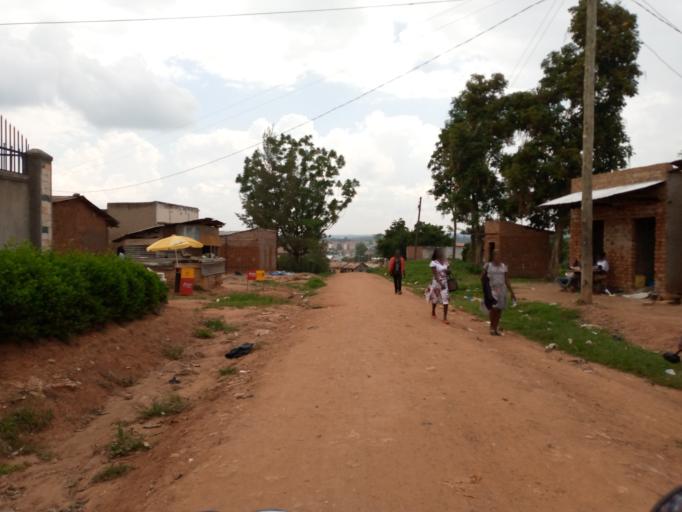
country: UG
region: Eastern Region
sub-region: Mbale District
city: Mbale
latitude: 1.0833
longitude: 34.1683
